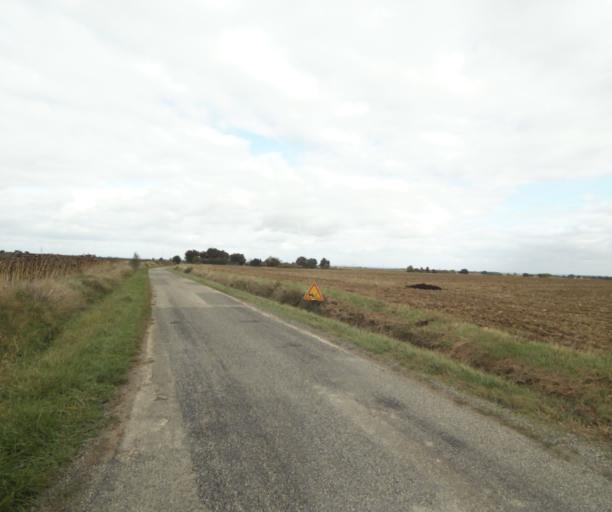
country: FR
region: Midi-Pyrenees
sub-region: Departement du Tarn-et-Garonne
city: Beaumont-de-Lomagne
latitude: 43.8865
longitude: 1.0939
